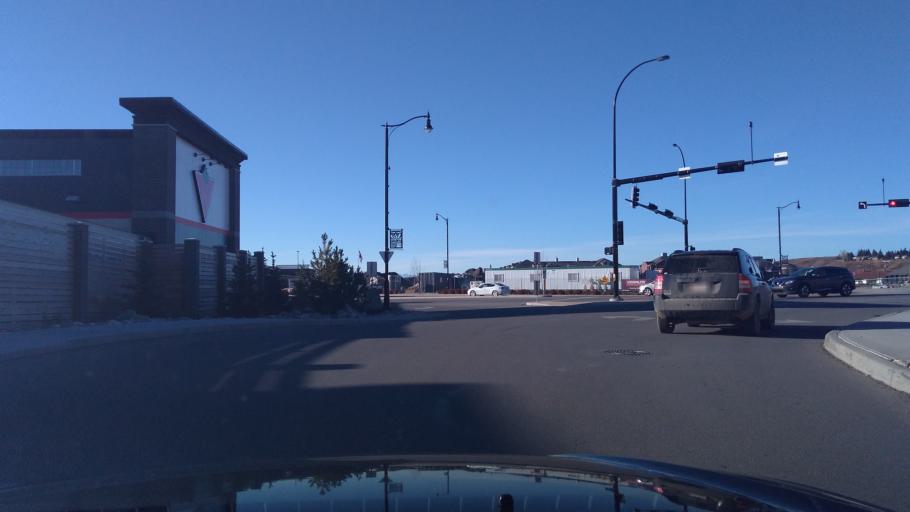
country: CA
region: Alberta
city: Cochrane
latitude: 51.1863
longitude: -114.4685
